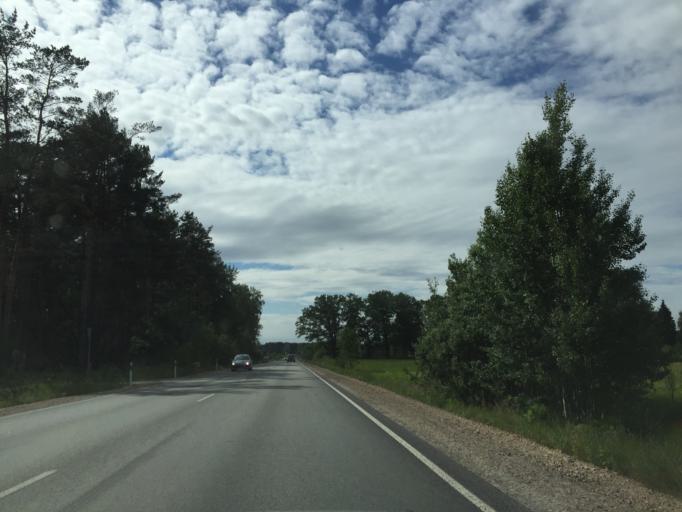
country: LV
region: Salaspils
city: Salaspils
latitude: 56.8989
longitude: 24.4230
